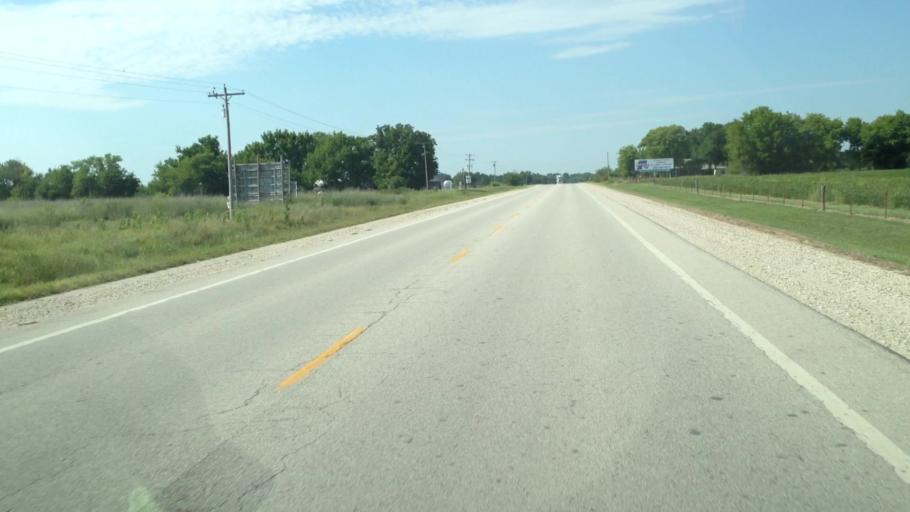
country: US
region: Kansas
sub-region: Neosho County
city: Erie
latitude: 37.5203
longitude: -95.2701
